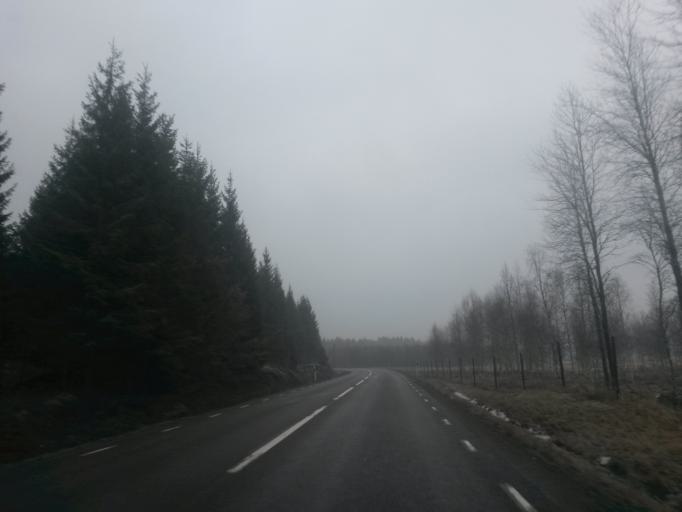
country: SE
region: Vaestra Goetaland
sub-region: Alingsas Kommun
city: Sollebrunn
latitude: 58.1798
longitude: 12.4213
